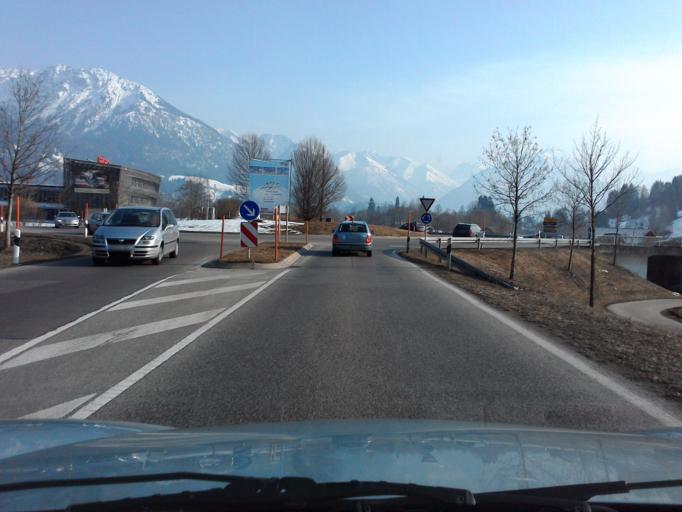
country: DE
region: Bavaria
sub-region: Swabia
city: Oberstdorf
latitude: 47.4246
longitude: 10.2676
